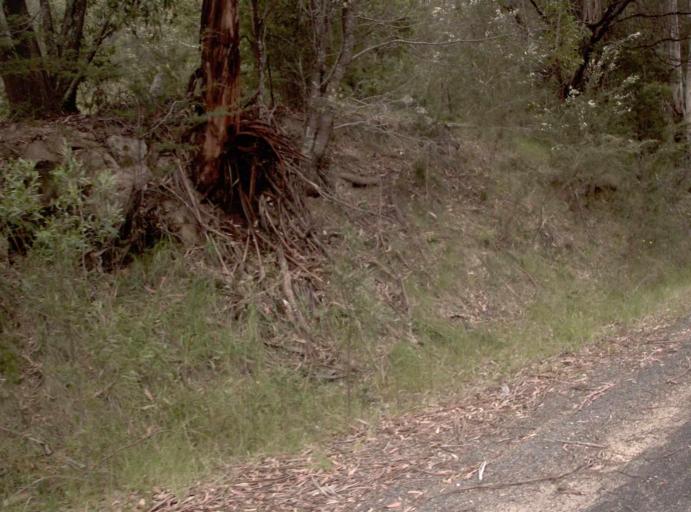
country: AU
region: New South Wales
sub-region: Bombala
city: Bombala
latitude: -37.2839
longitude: 149.2220
